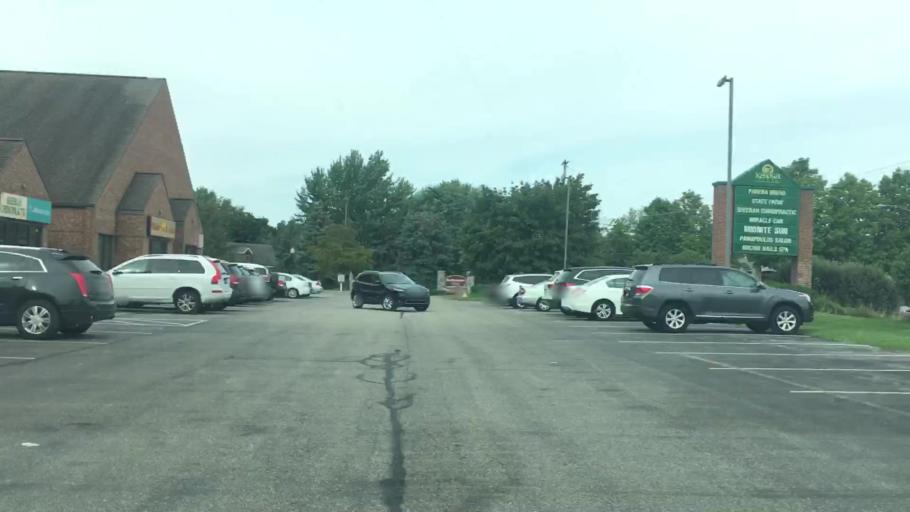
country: US
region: Michigan
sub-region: Ottawa County
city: Jenison
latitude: 42.8849
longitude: -85.7828
